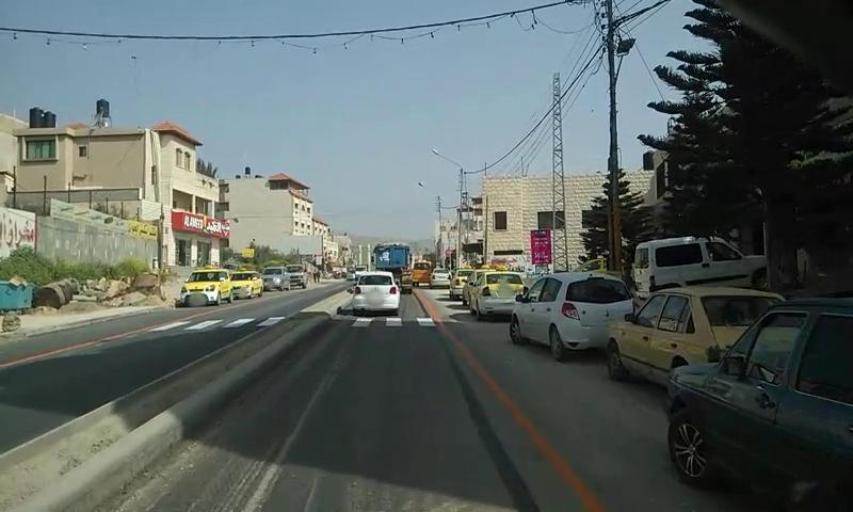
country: PS
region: West Bank
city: Huwwarah
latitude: 32.1507
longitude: 35.2584
